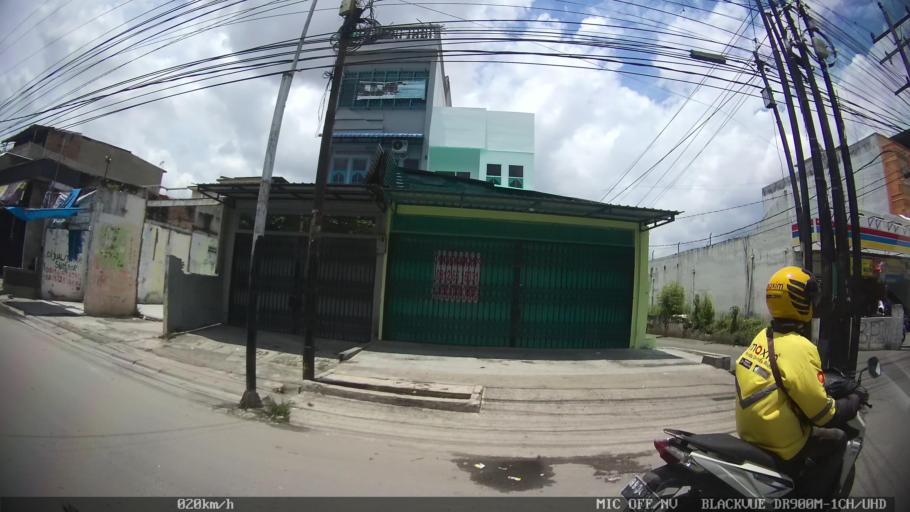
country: ID
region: North Sumatra
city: Medan
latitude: 3.6004
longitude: 98.7066
